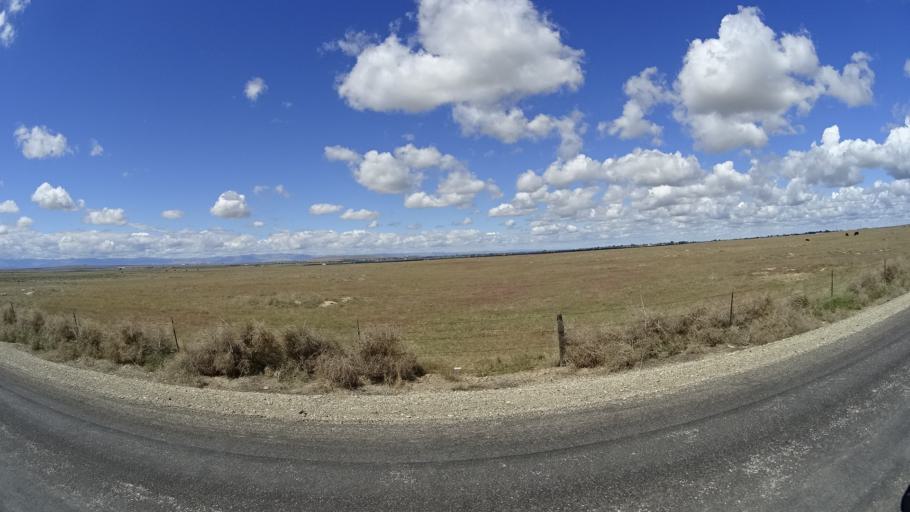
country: US
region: Idaho
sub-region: Ada County
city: Kuna
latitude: 43.4672
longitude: -116.2744
